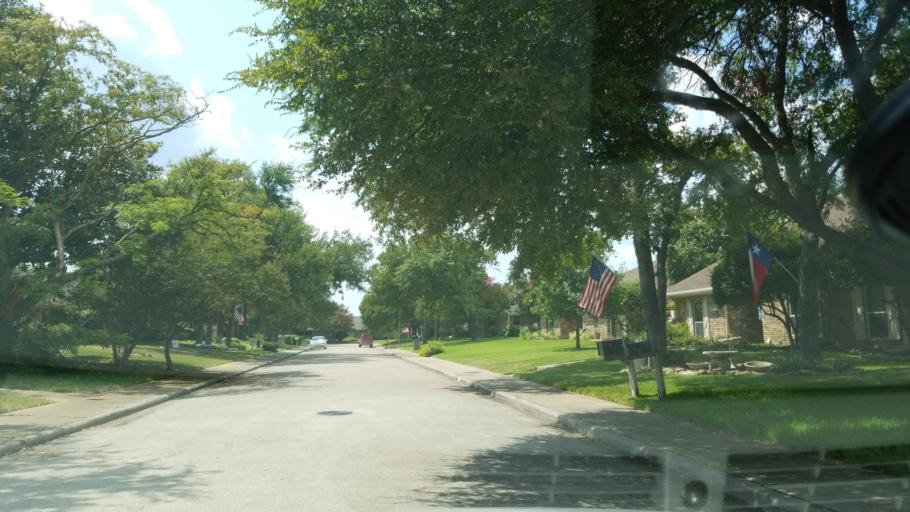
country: US
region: Texas
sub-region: Dallas County
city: Richardson
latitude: 32.9146
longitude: -96.7196
